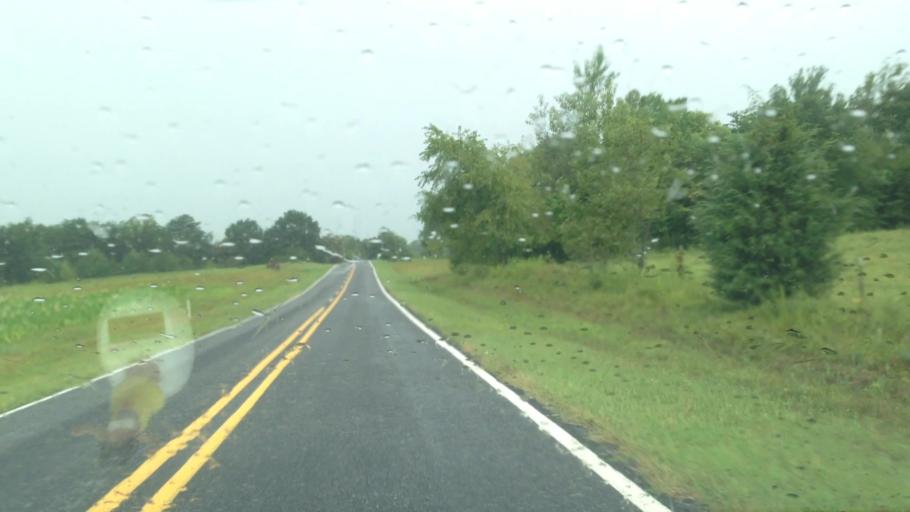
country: US
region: North Carolina
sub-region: Stokes County
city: Danbury
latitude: 36.4458
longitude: -80.0953
